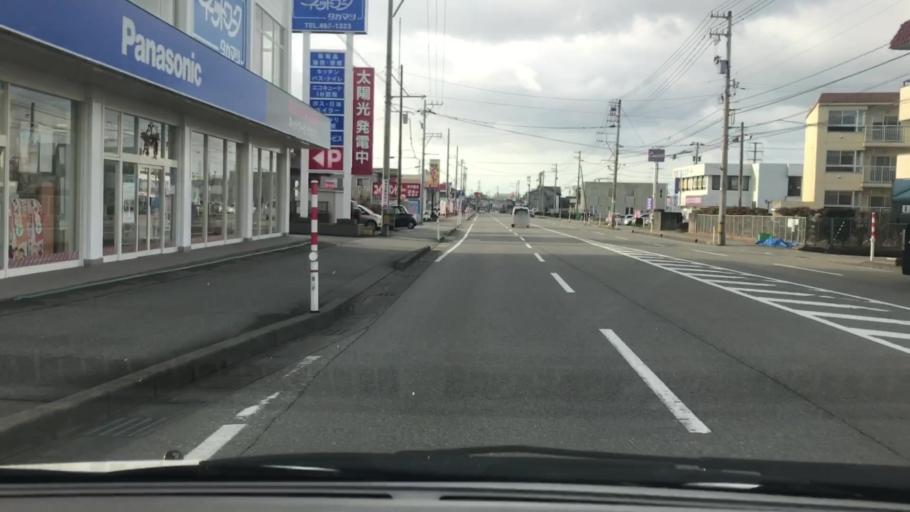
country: JP
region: Toyama
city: Toyama-shi
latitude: 36.6848
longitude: 137.2469
